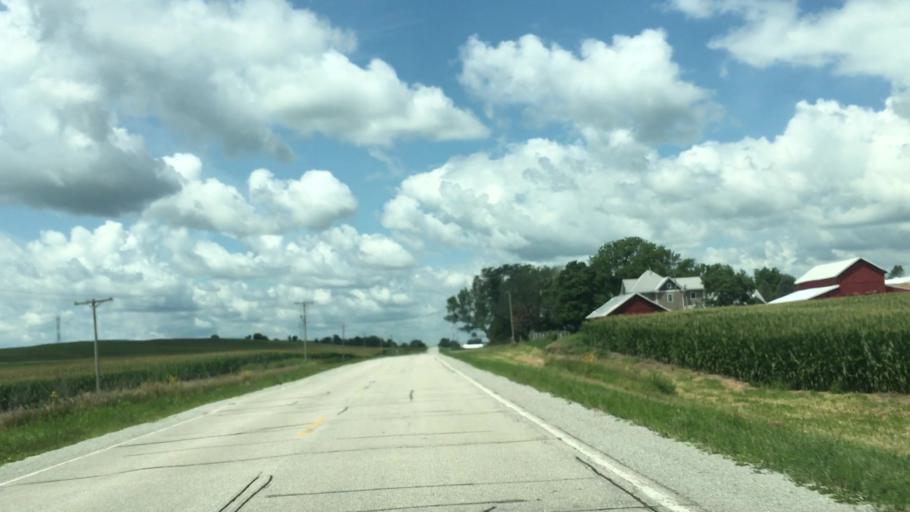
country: US
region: Iowa
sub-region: Johnson County
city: Solon
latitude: 41.8310
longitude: -91.4757
